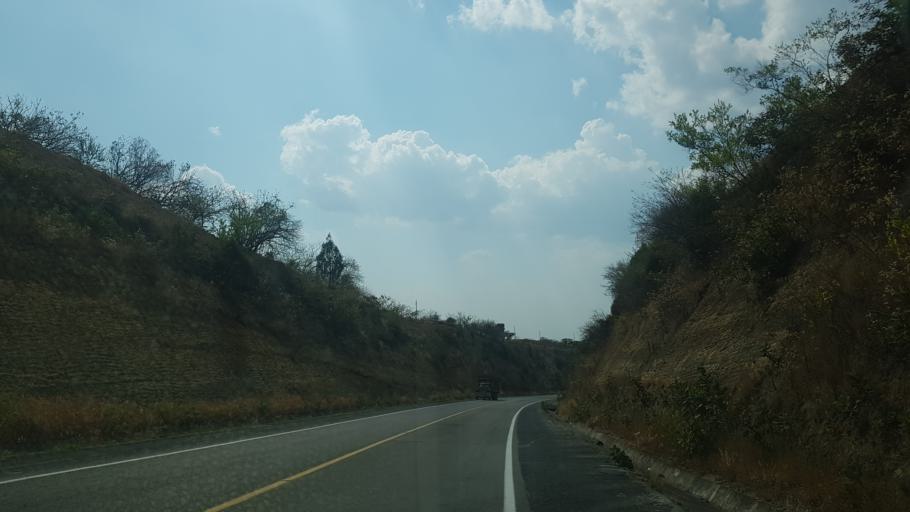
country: MX
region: Puebla
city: San Juan Amecac
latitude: 18.8157
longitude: -98.6759
